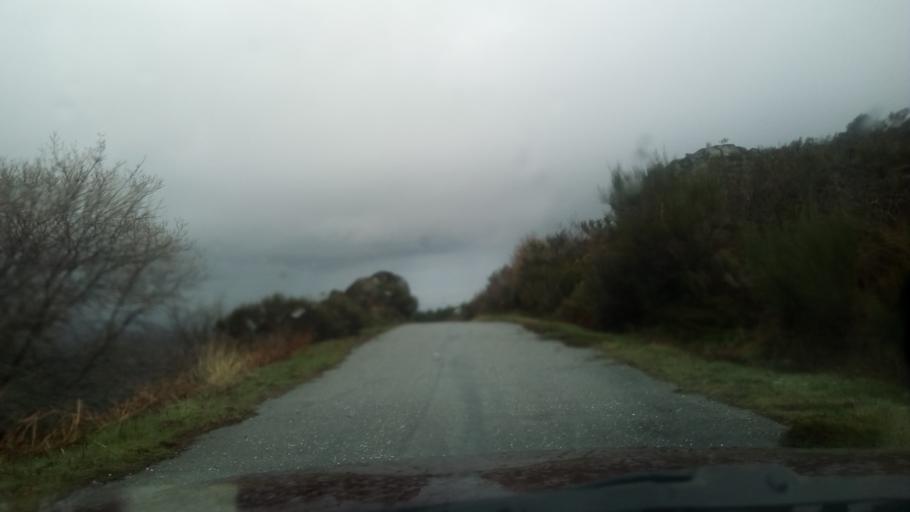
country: PT
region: Guarda
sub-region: Celorico da Beira
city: Celorico da Beira
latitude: 40.5226
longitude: -7.4529
